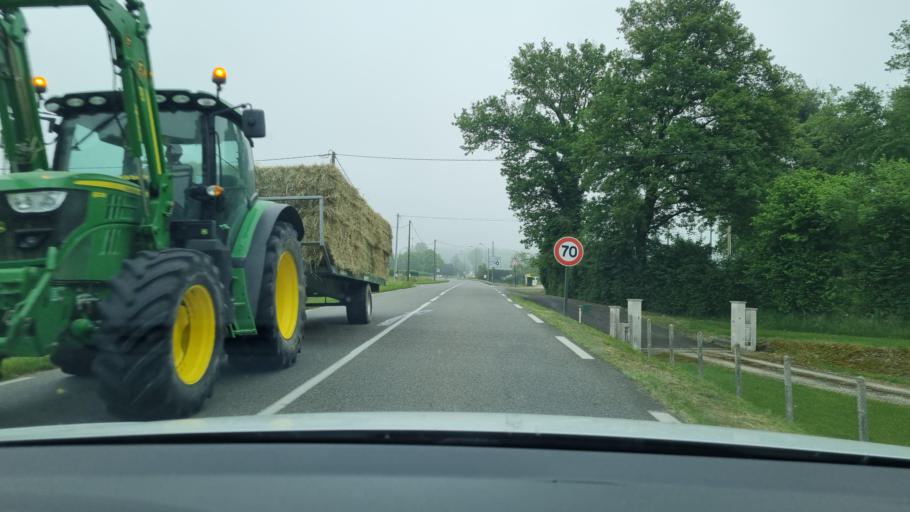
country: FR
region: Aquitaine
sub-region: Departement des Landes
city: Amou
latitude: 43.5403
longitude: -0.6838
